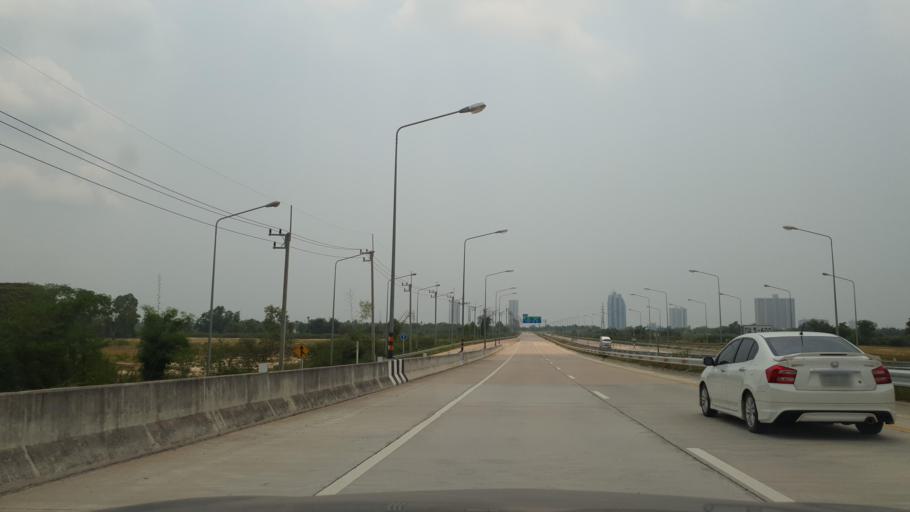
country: TH
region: Chon Buri
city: Phatthaya
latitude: 12.8363
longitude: 100.9343
